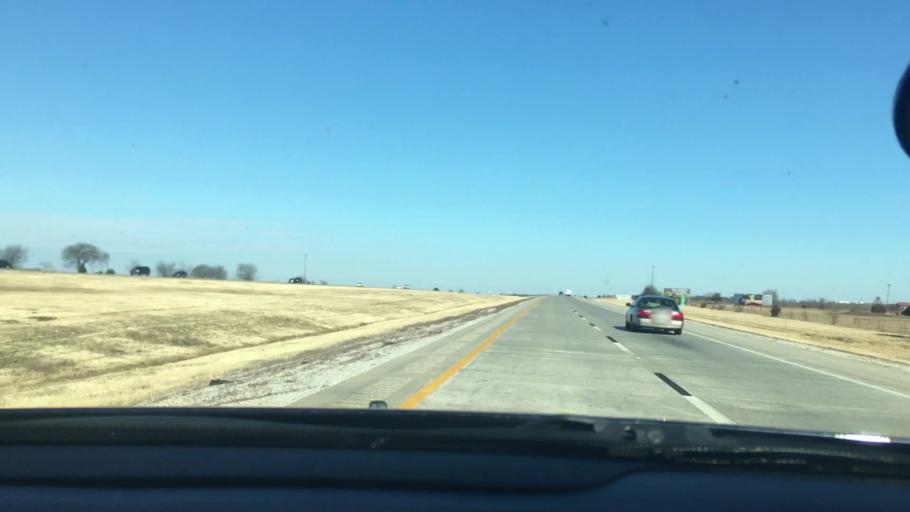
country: US
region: Oklahoma
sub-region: Carter County
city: Ardmore
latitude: 34.0929
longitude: -97.1505
